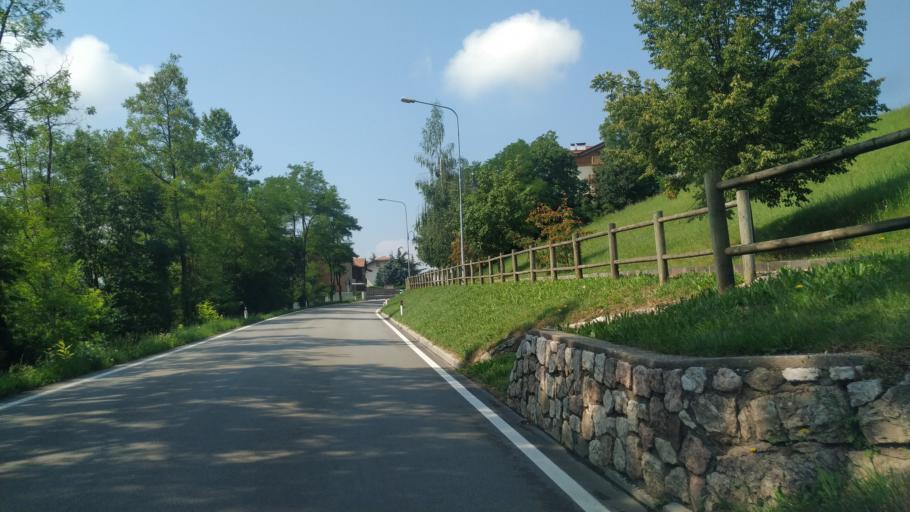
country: IT
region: Trentino-Alto Adige
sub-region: Provincia di Trento
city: Romeno
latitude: 46.3989
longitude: 11.1265
